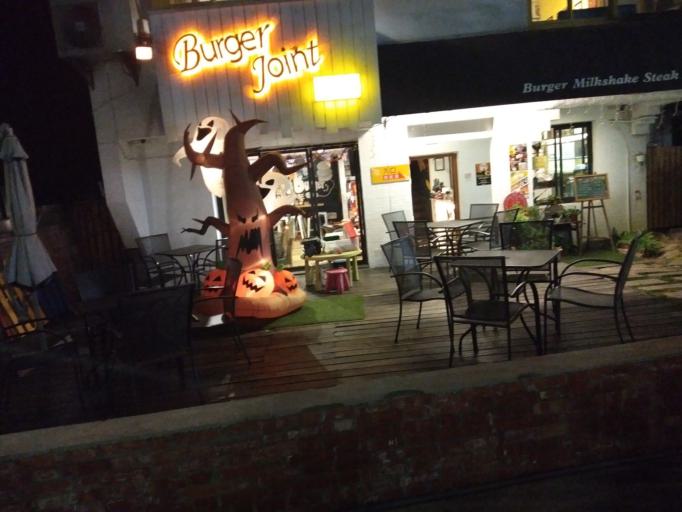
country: TW
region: Taiwan
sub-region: Taichung City
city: Taichung
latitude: 24.1844
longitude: 120.6172
